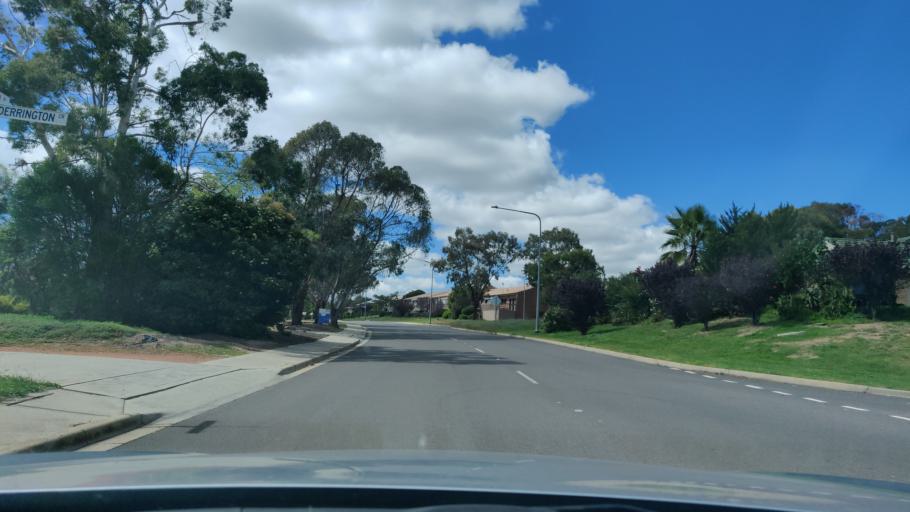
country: AU
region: Australian Capital Territory
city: Macarthur
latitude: -35.4323
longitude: 149.0773
